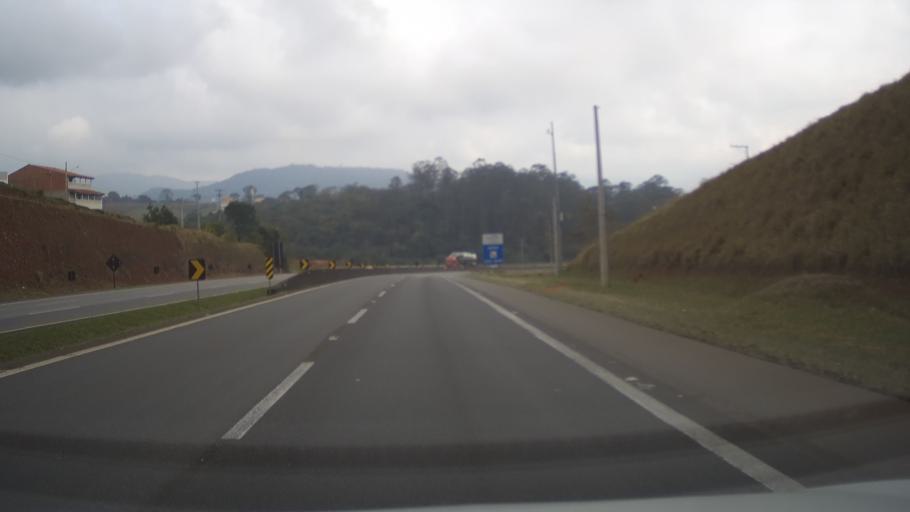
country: BR
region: Minas Gerais
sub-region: Extrema
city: Extrema
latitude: -22.8530
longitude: -46.3373
